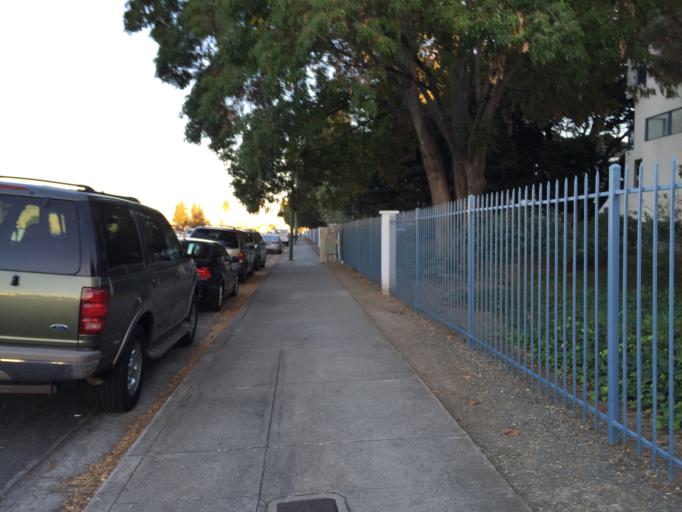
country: US
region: California
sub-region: Santa Clara County
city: Santa Clara
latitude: 37.3230
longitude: -121.9866
